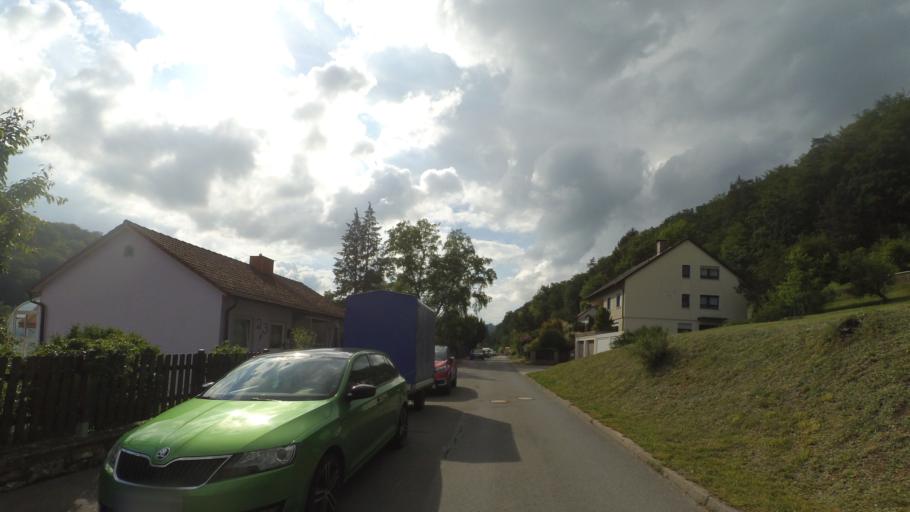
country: DE
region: Bavaria
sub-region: Upper Franconia
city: Bad Berneck im Fichtelgebirge
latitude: 50.0383
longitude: 11.6795
